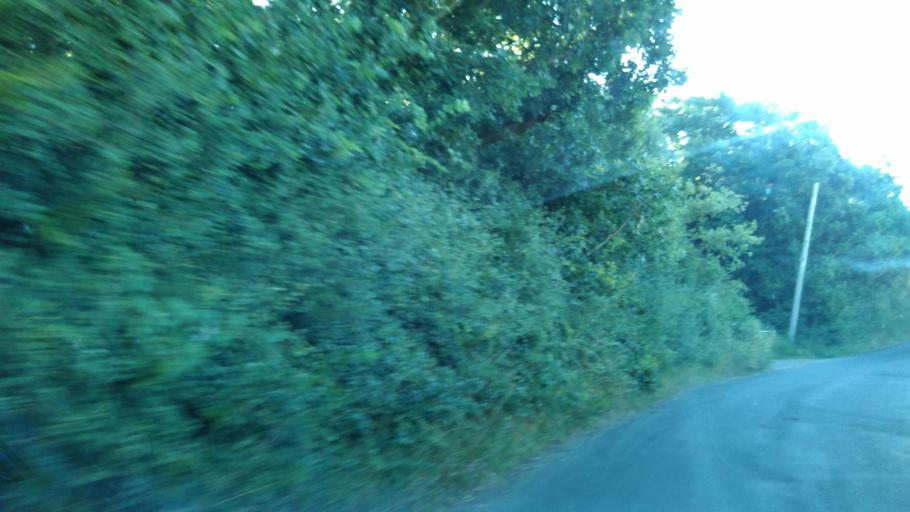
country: GB
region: England
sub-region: Kent
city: Blean
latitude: 51.3168
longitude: 1.0151
